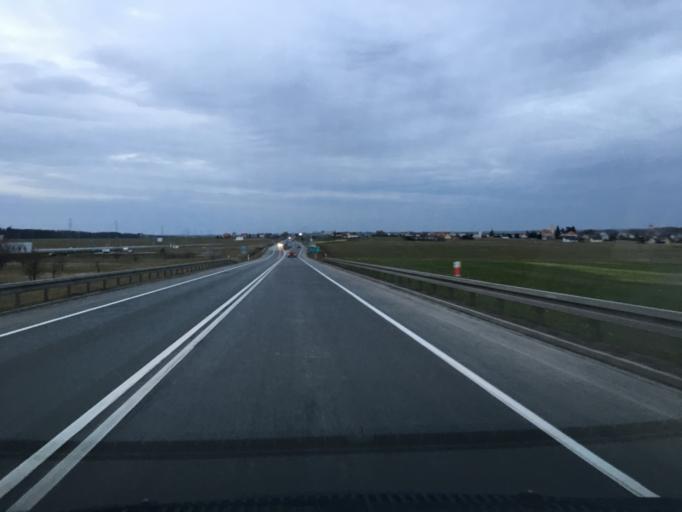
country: PL
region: Opole Voivodeship
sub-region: Powiat opolski
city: Proszkow
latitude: 50.5292
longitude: 17.9193
